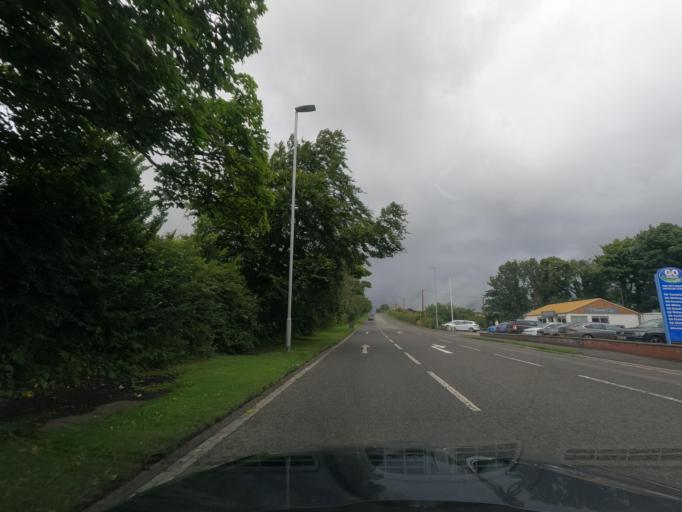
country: GB
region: England
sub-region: Northumberland
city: Berwick-Upon-Tweed
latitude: 55.7447
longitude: -1.9972
